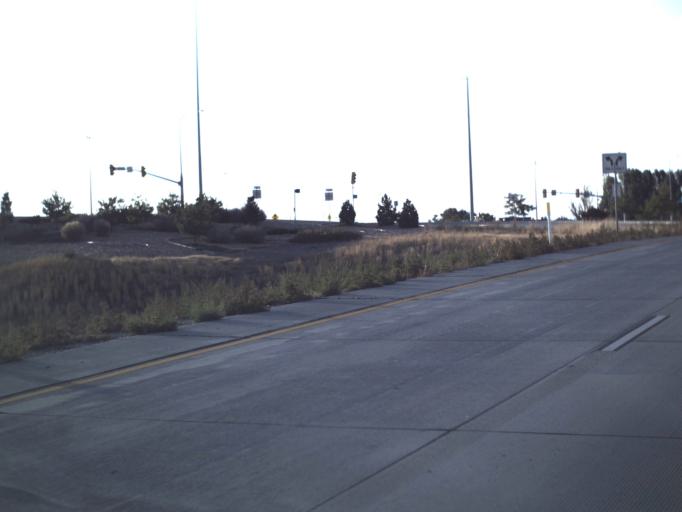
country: US
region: Utah
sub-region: Utah County
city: American Fork
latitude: 40.3605
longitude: -111.7839
